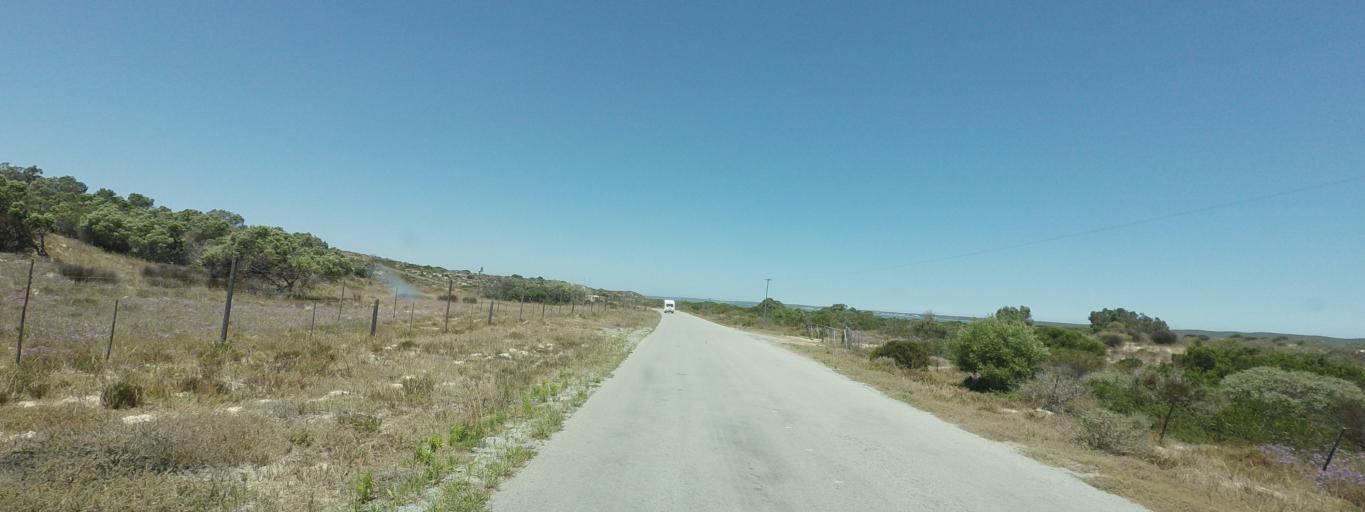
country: ZA
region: Western Cape
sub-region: West Coast District Municipality
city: Saldanha
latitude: -33.1159
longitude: 18.0537
